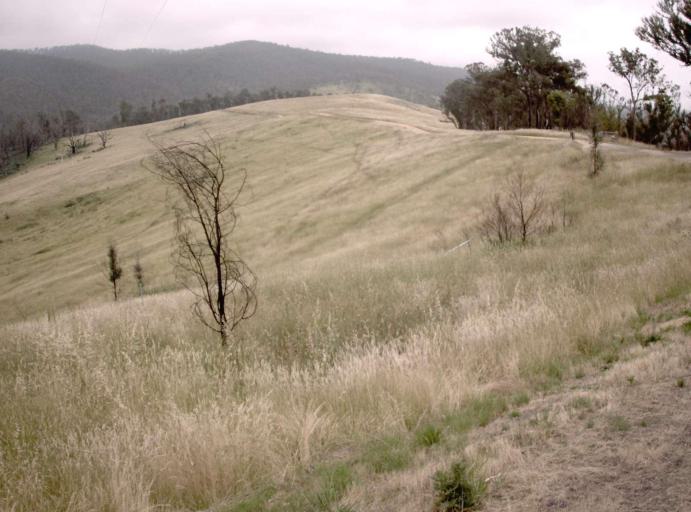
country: AU
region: Victoria
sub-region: Wellington
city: Heyfield
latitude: -37.8276
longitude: 146.6776
